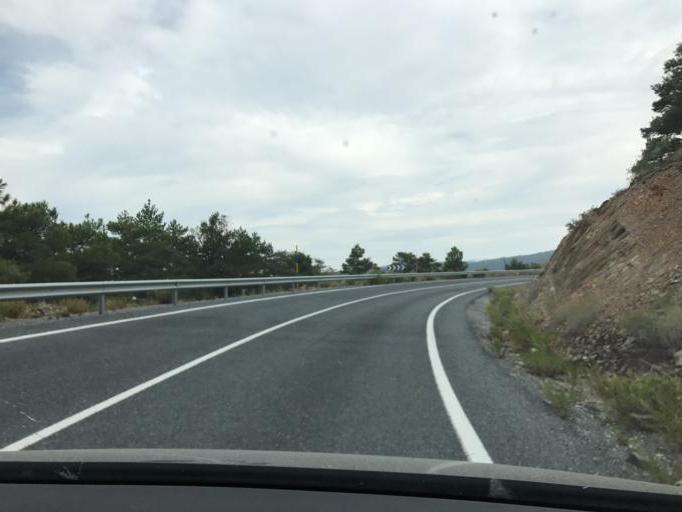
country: ES
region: Andalusia
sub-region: Provincia de Granada
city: Ferreira
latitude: 37.1472
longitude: -3.0463
